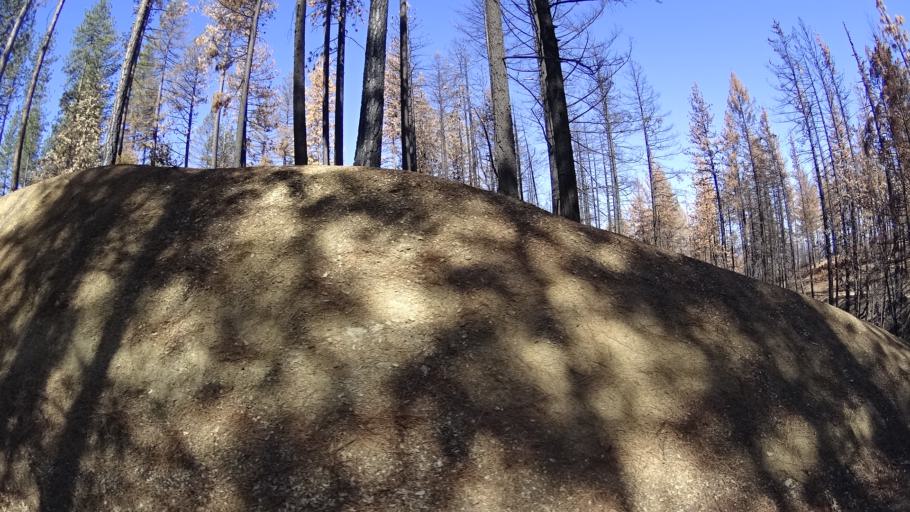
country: US
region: California
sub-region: Tehama County
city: Rancho Tehama Reserve
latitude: 39.6589
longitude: -122.7169
